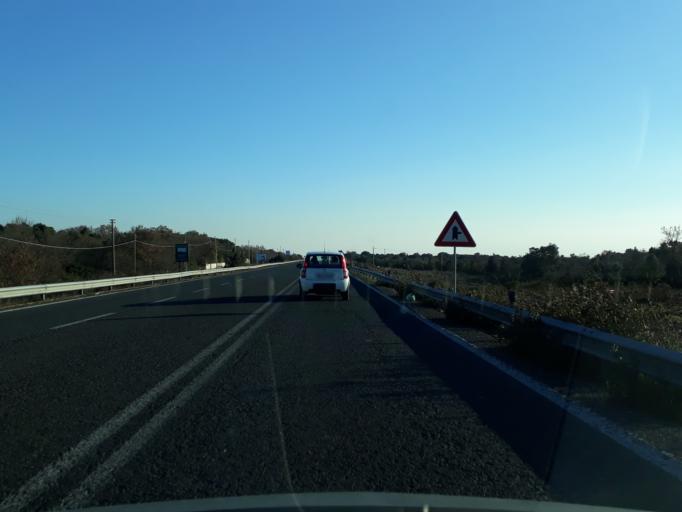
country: IT
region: Apulia
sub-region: Provincia di Taranto
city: Martina Franca
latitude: 40.6376
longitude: 17.3146
